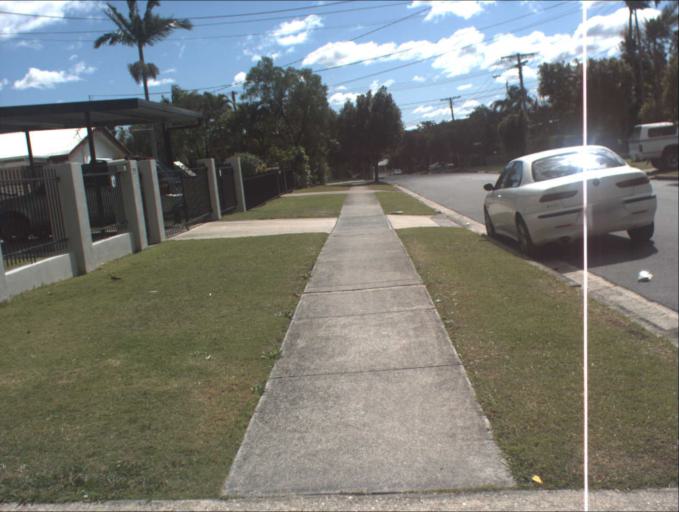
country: AU
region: Queensland
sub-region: Logan
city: Waterford West
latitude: -27.6733
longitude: 153.1056
